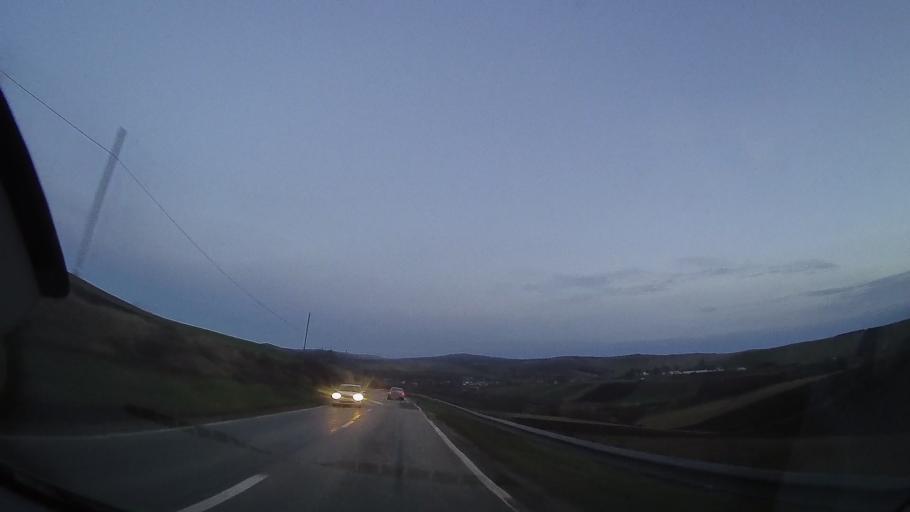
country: RO
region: Cluj
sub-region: Comuna Camarasu
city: Camarasu
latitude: 46.7937
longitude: 24.1121
